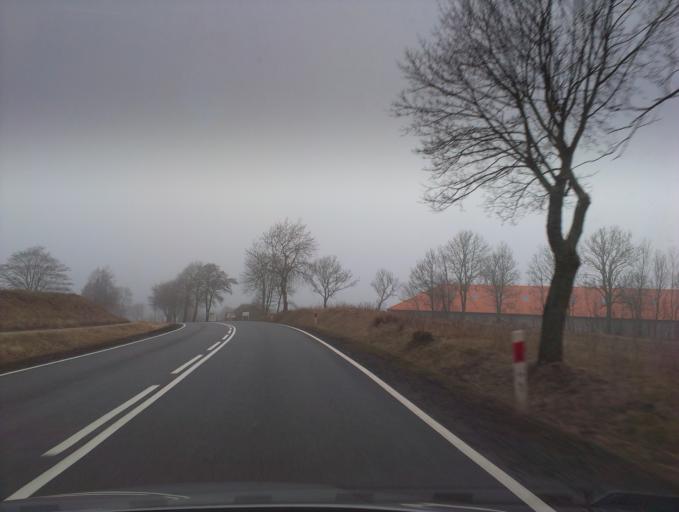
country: PL
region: West Pomeranian Voivodeship
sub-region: Powiat szczecinecki
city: Szczecinek
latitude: 53.7477
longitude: 16.6553
